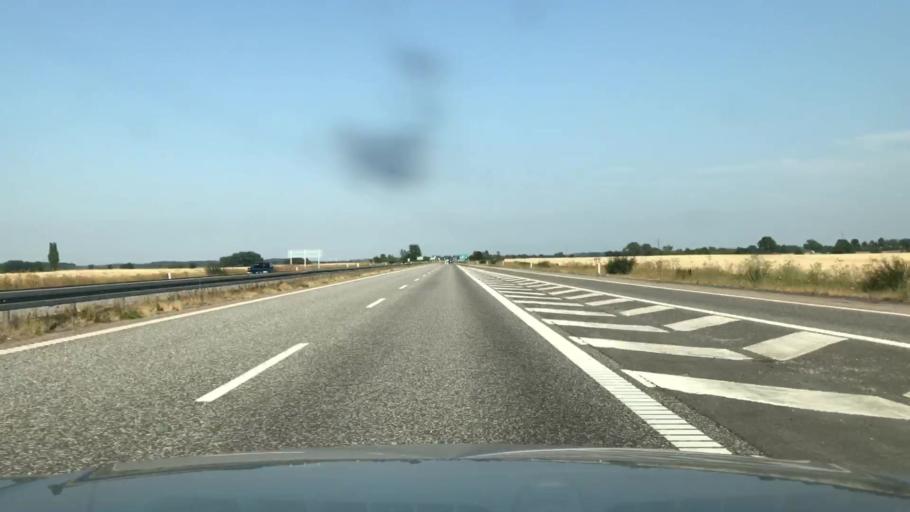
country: DK
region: Zealand
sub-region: Guldborgsund Kommune
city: Sundby
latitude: 54.8280
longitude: 11.7453
